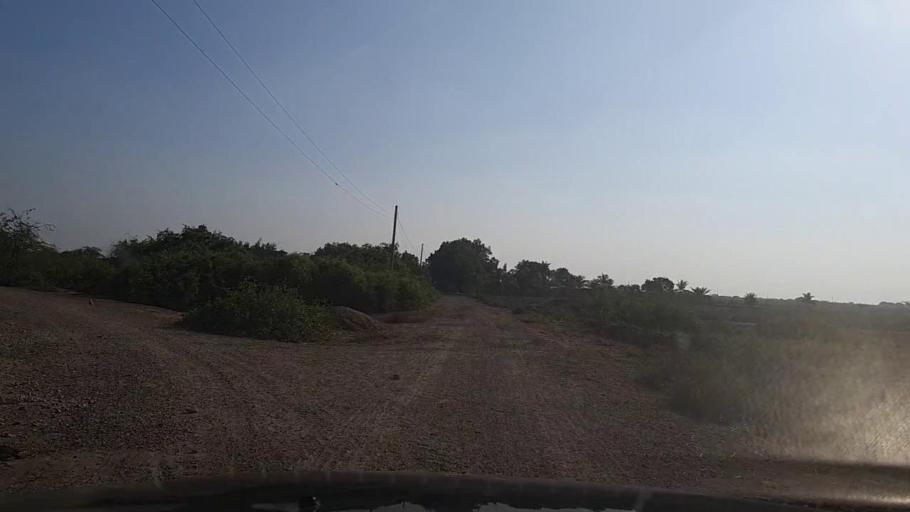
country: PK
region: Sindh
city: Gharo
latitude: 24.7056
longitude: 67.7042
